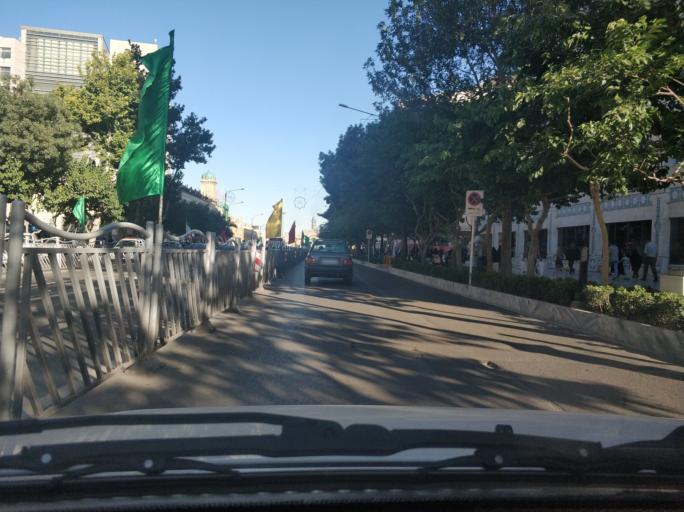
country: IR
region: Razavi Khorasan
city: Mashhad
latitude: 36.2926
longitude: 59.6114
